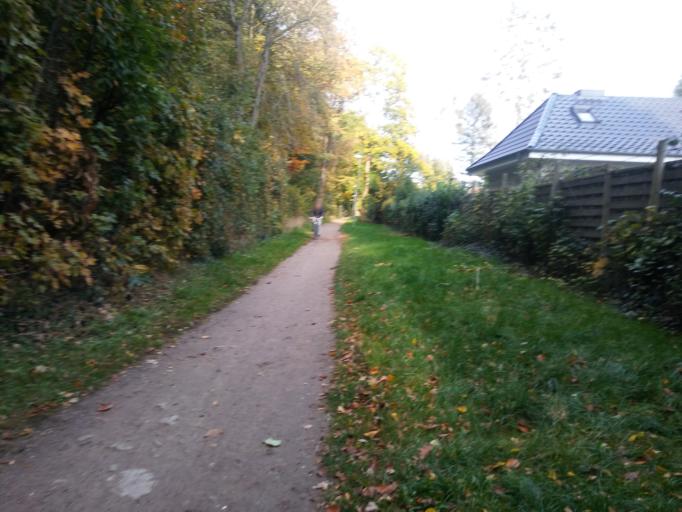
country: DE
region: Schleswig-Holstein
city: Neumunster
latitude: 54.0589
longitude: 9.9611
